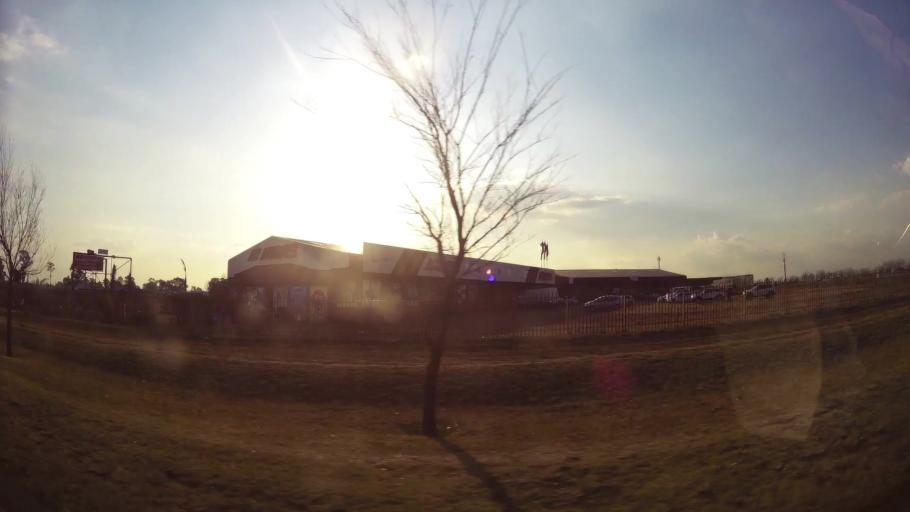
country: ZA
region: Gauteng
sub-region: Ekurhuleni Metropolitan Municipality
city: Germiston
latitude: -26.3362
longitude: 28.2294
